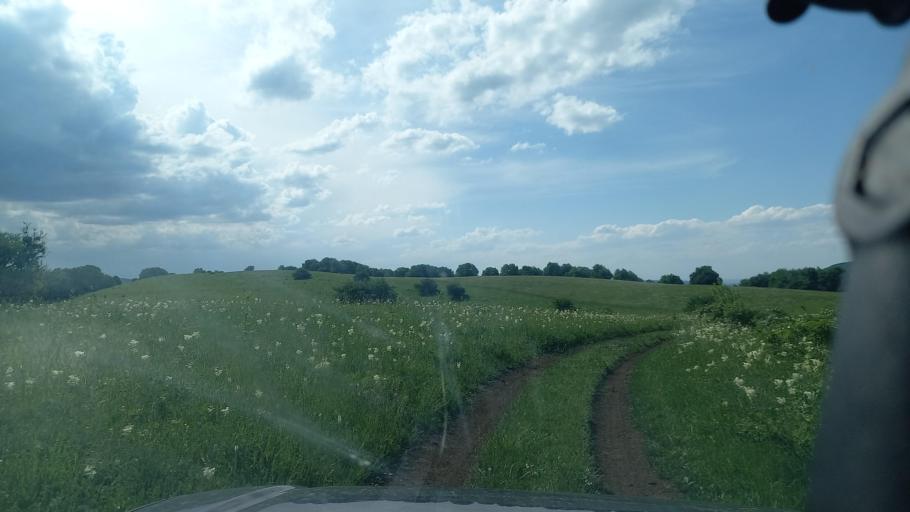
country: RU
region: Karachayevo-Cherkesiya
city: Kurdzhinovo
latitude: 44.1246
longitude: 41.0894
